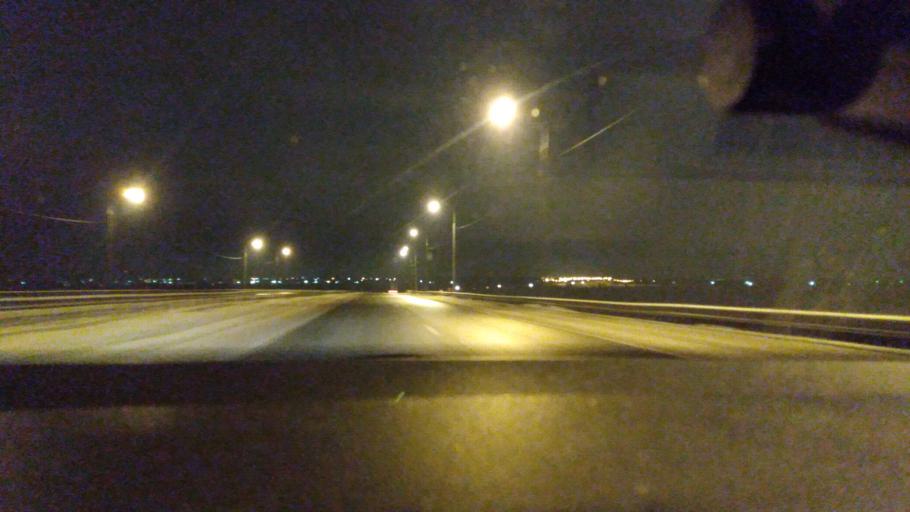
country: RU
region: Moskovskaya
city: Raduzhnyy
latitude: 55.1412
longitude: 38.7494
